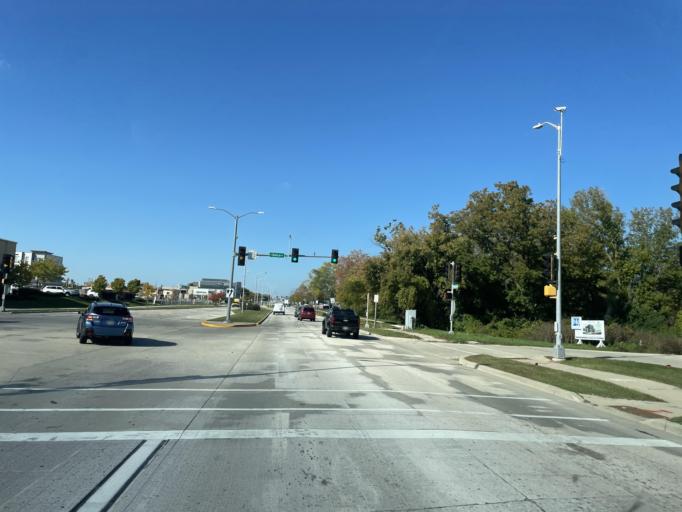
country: US
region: Wisconsin
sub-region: Milwaukee County
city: Oak Creek
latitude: 42.9013
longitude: -87.9150
